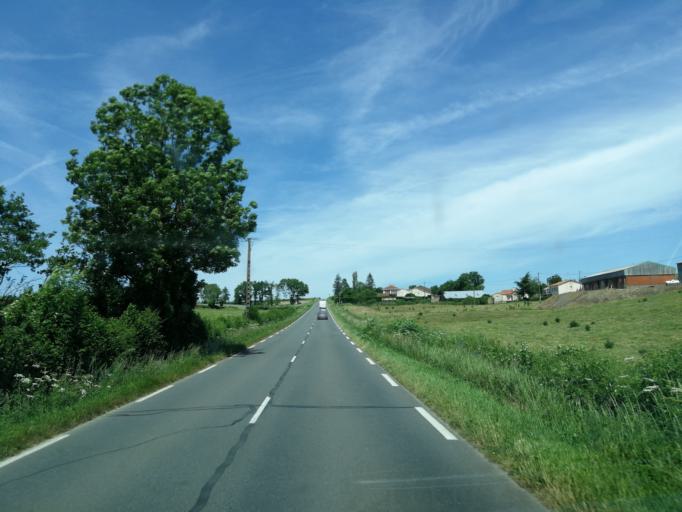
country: FR
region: Pays de la Loire
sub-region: Departement de la Vendee
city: La Tardiere
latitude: 46.6735
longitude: -0.7201
